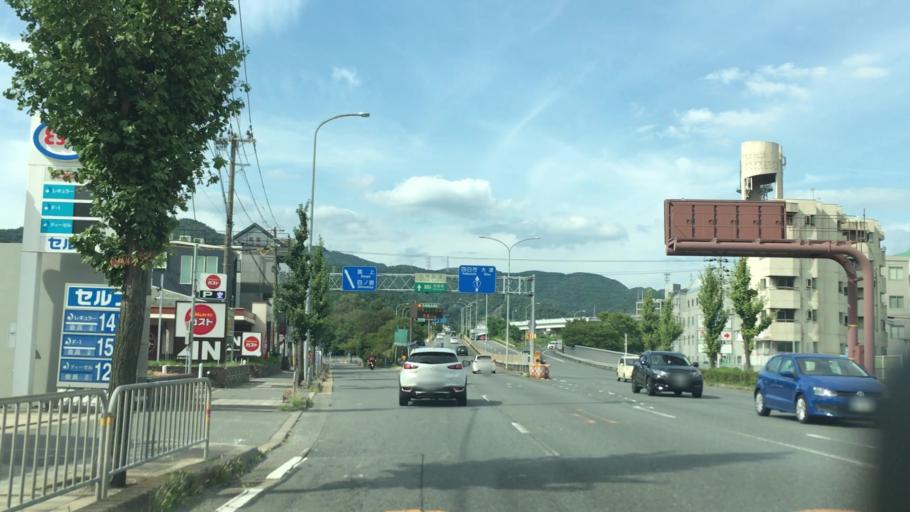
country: JP
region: Shiga Prefecture
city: Otsu-shi
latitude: 34.9866
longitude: 135.8278
